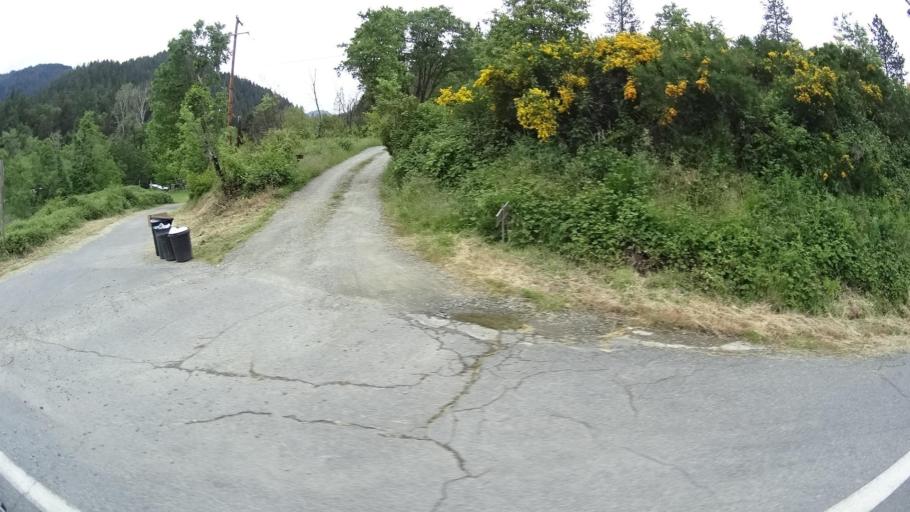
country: US
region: California
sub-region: Humboldt County
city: Willow Creek
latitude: 41.2969
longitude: -123.5564
